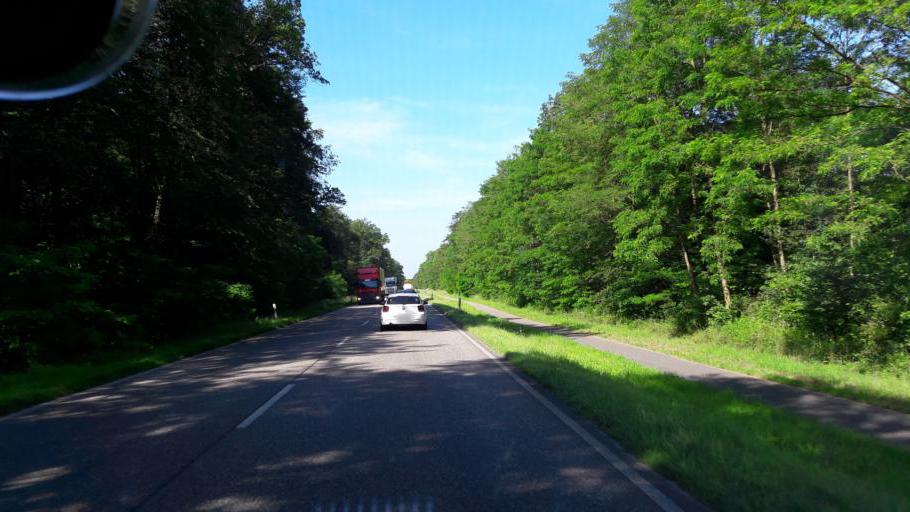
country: DE
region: Baden-Wuerttemberg
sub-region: Karlsruhe Region
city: Muggensturm
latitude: 48.8934
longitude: 8.2895
